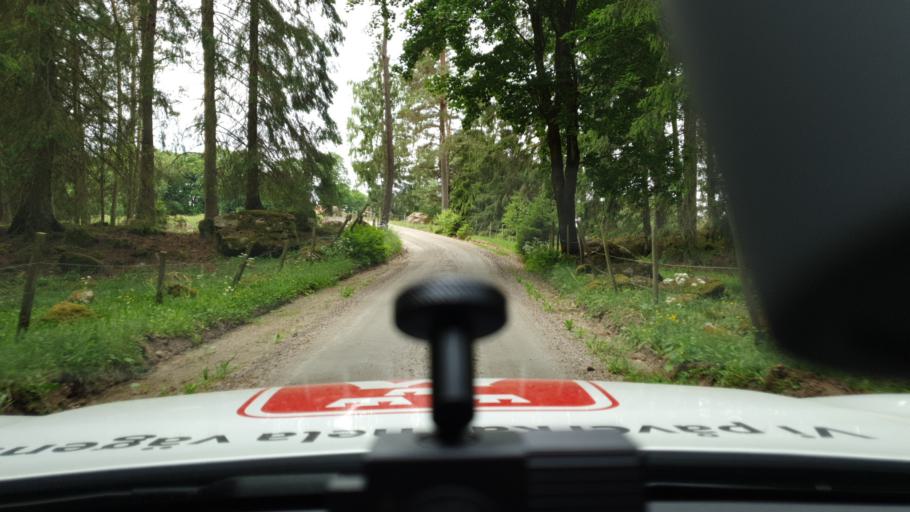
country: SE
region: Vaestra Goetaland
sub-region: Falkopings Kommun
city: Falkoeping
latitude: 58.0385
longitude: 13.6560
